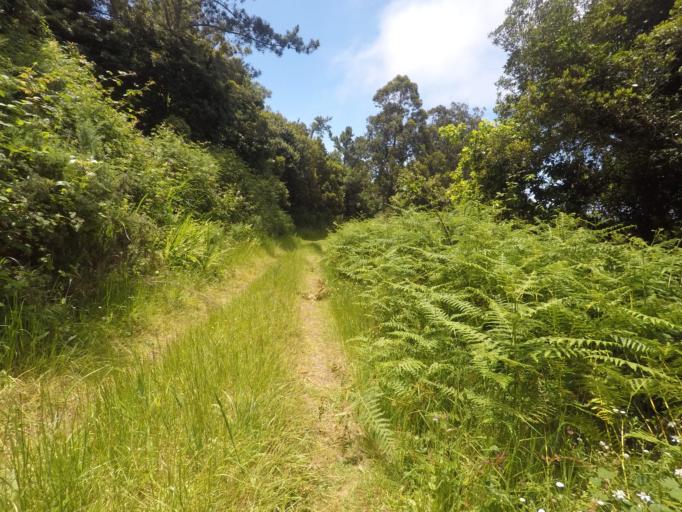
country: PT
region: Madeira
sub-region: Porto Moniz
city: Porto Moniz
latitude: 32.8388
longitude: -17.1457
